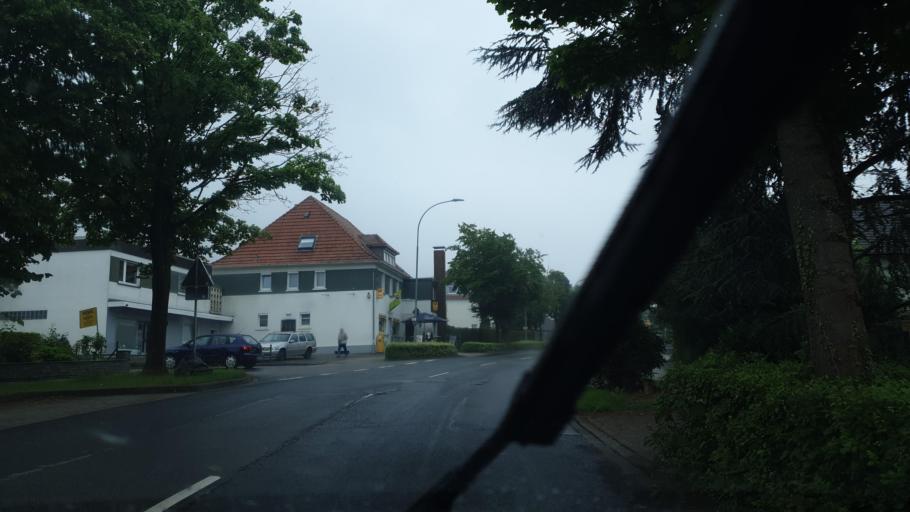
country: DE
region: North Rhine-Westphalia
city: Bad Oeynhausen
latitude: 52.1828
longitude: 8.8014
